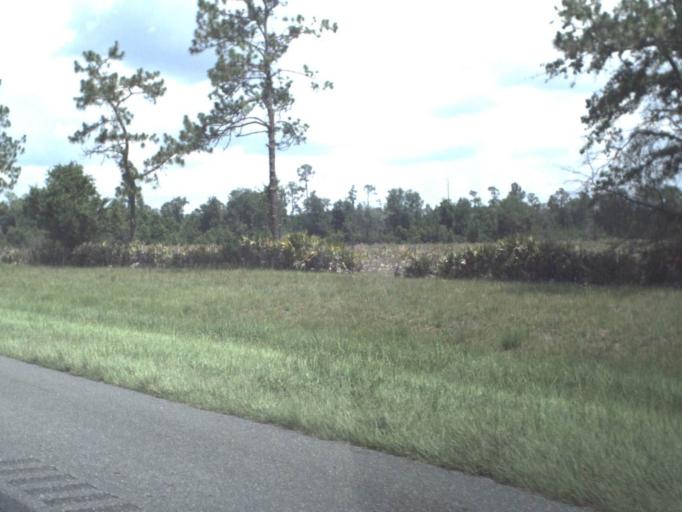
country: US
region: Florida
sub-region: Baker County
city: Macclenny
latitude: 30.2437
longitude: -82.3117
